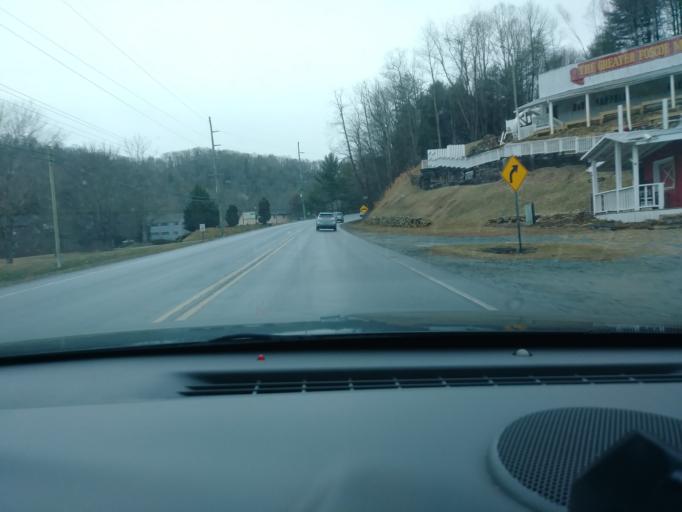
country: US
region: North Carolina
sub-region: Watauga County
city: Foscoe
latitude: 36.1570
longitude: -81.7726
